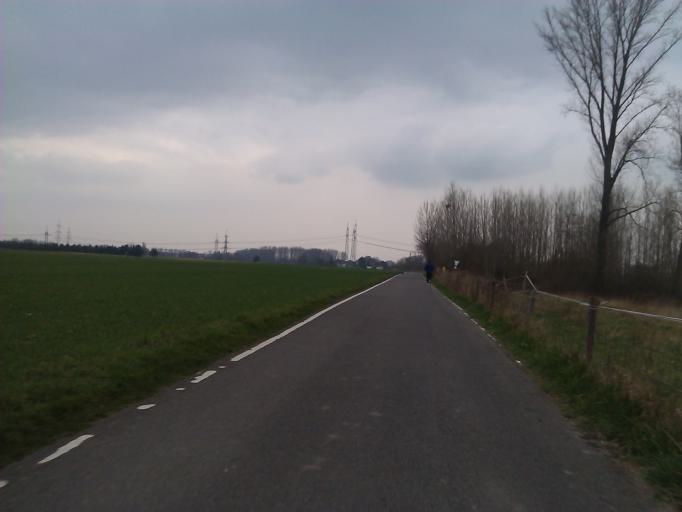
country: DE
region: North Rhine-Westphalia
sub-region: Regierungsbezirk Koln
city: Leverkusen
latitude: 51.0331
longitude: 6.9543
